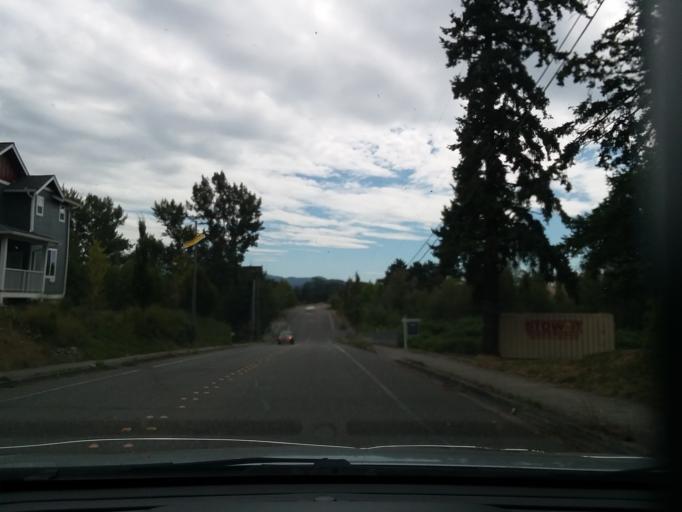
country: US
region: Washington
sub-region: Whatcom County
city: Bellingham
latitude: 48.7870
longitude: -122.4785
